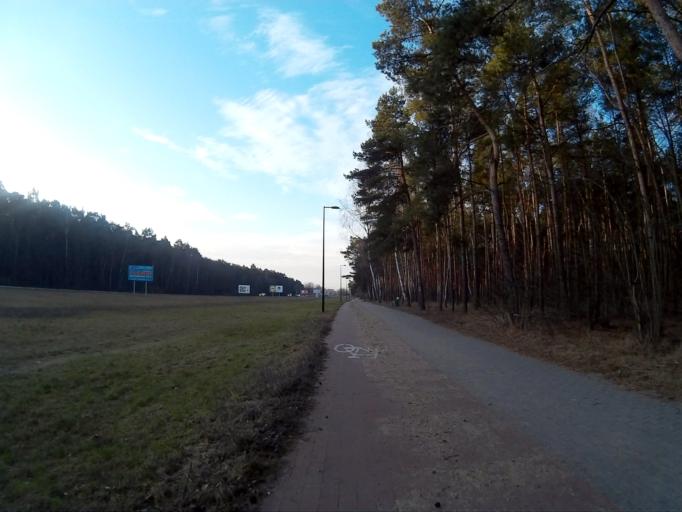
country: PL
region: Kujawsko-Pomorskie
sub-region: Bydgoszcz
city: Bydgoszcz
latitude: 53.1530
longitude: 18.0306
